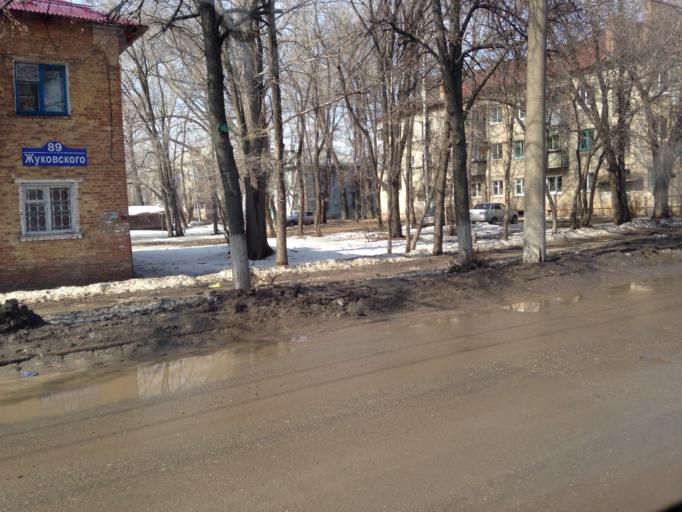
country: RU
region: Ulyanovsk
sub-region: Ulyanovskiy Rayon
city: Ulyanovsk
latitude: 54.3499
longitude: 48.5481
